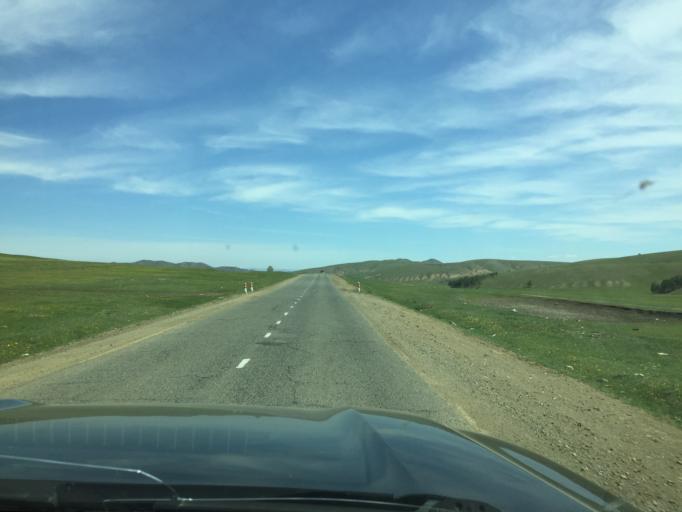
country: MN
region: Central Aimak
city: Javhlant
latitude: 48.6566
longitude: 106.1150
